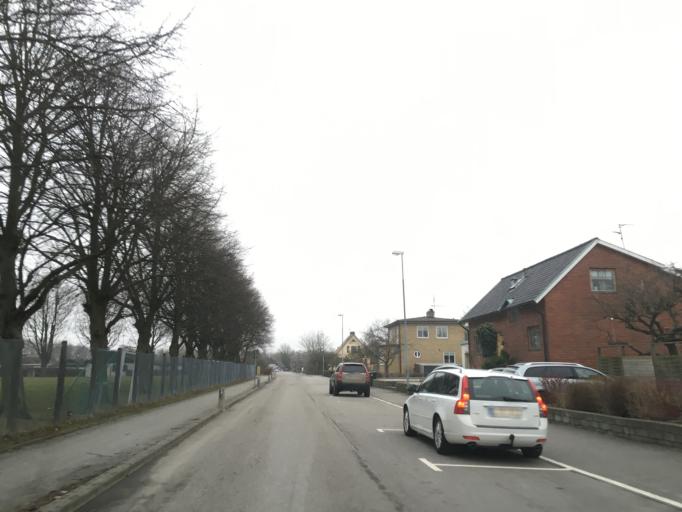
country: SE
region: Skane
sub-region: Lomma Kommun
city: Lomma
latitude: 55.6658
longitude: 13.0666
